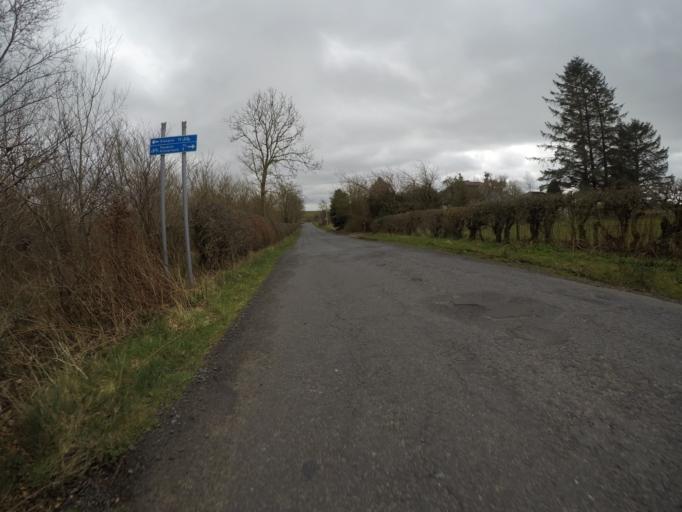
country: GB
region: Scotland
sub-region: East Ayrshire
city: Stewarton
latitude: 55.6745
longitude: -4.4390
